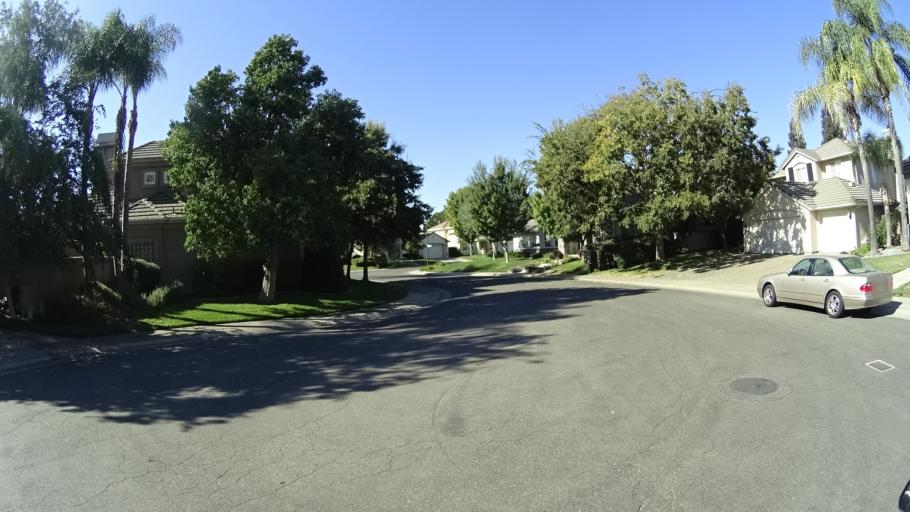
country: US
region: California
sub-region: Sacramento County
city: Parkway
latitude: 38.4845
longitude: -121.5277
